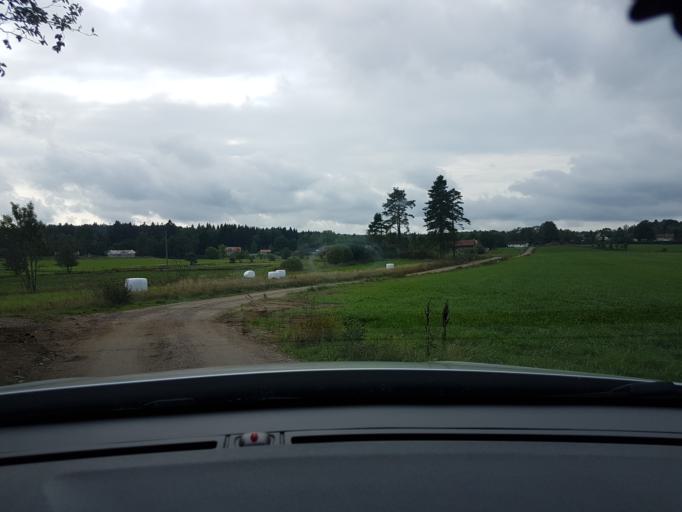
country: SE
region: Vaestra Goetaland
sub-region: Ale Kommun
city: Skepplanda
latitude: 57.8929
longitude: 12.2033
